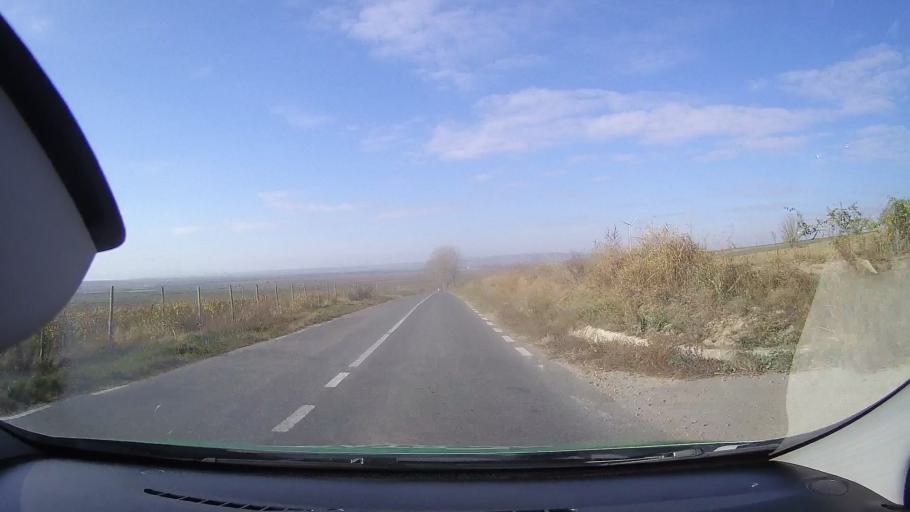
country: RO
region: Tulcea
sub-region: Comuna Valea Nucarilor
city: Iazurile
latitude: 45.0247
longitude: 28.9798
